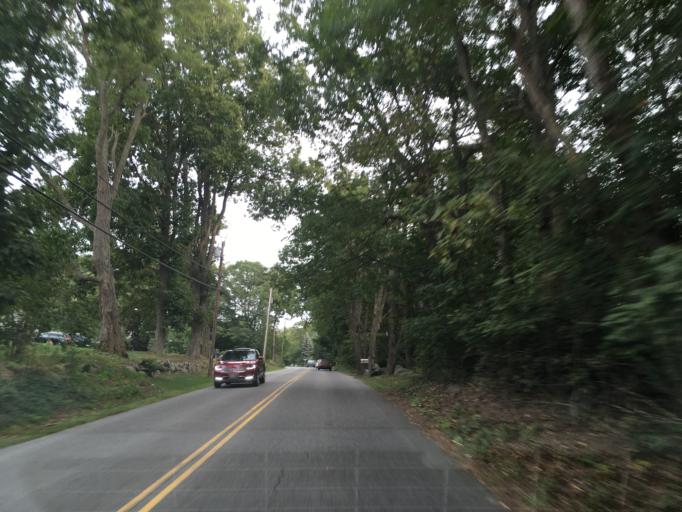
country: US
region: New Hampshire
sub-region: Rockingham County
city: Exeter
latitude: 42.9906
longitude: -70.9185
